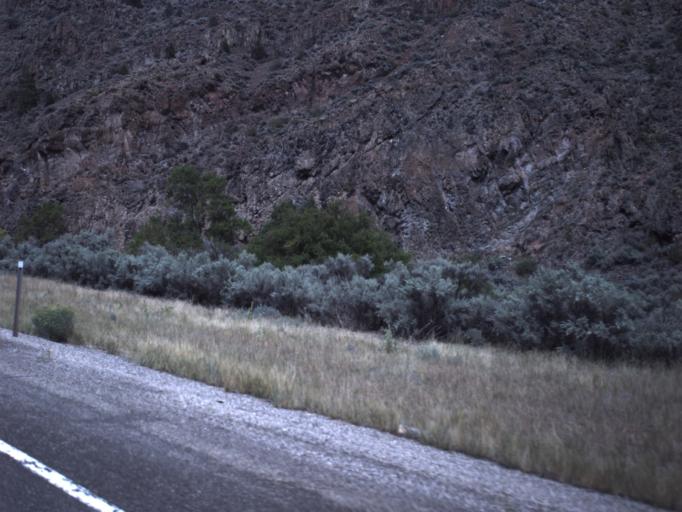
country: US
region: Utah
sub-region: Piute County
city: Junction
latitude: 38.1076
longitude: -112.3361
